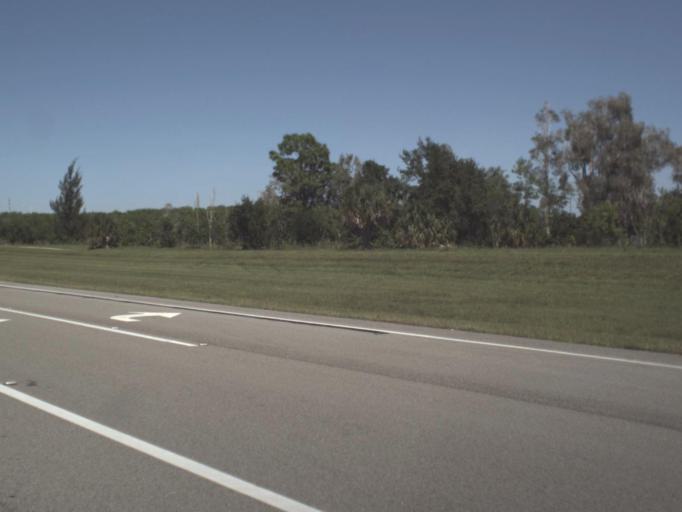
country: US
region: Florida
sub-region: Lee County
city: San Carlos Park
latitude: 26.4885
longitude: -81.8426
